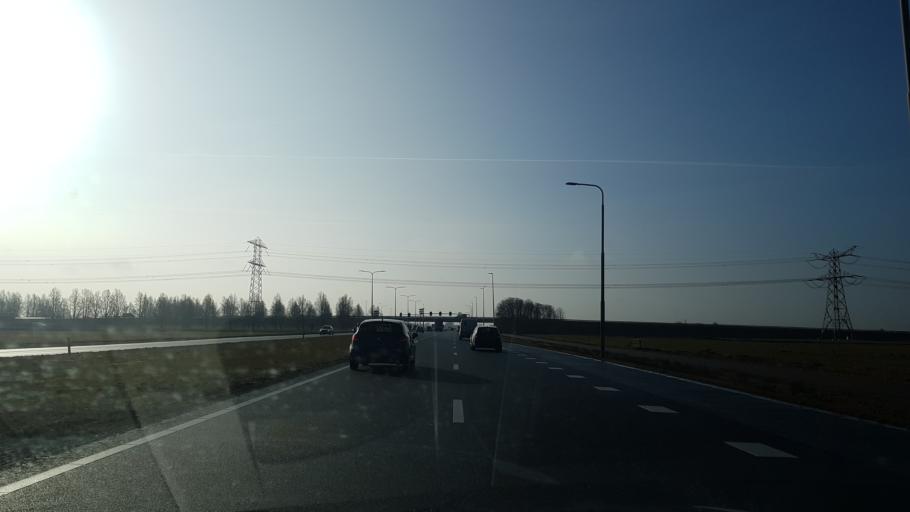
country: NL
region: Friesland
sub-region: Gemeente Boarnsterhim
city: Wergea
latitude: 53.1702
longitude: 5.8276
